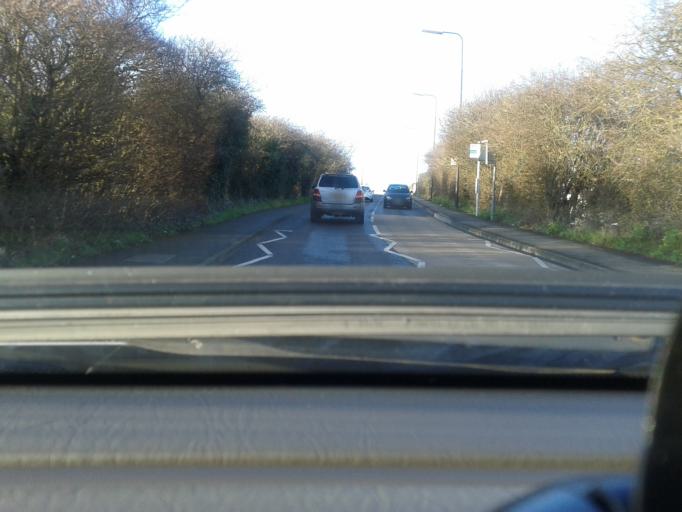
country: GB
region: England
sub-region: North Somerset
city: St. Georges
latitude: 51.3555
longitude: -2.9115
